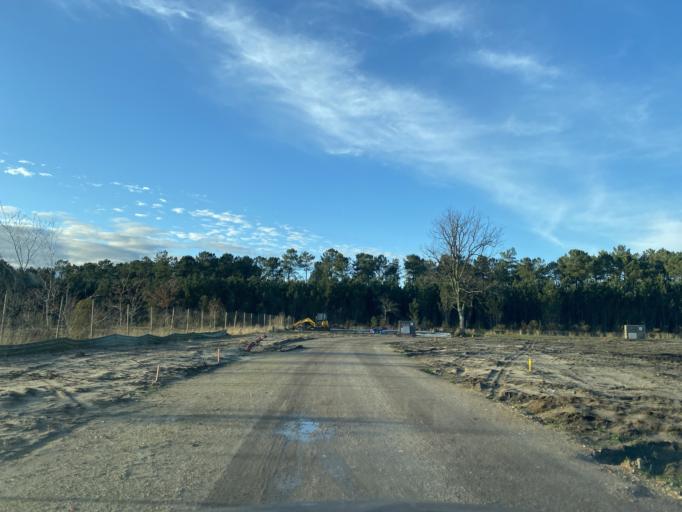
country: FR
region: Aquitaine
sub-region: Departement de la Gironde
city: Marcheprime
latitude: 44.7009
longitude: -0.8502
